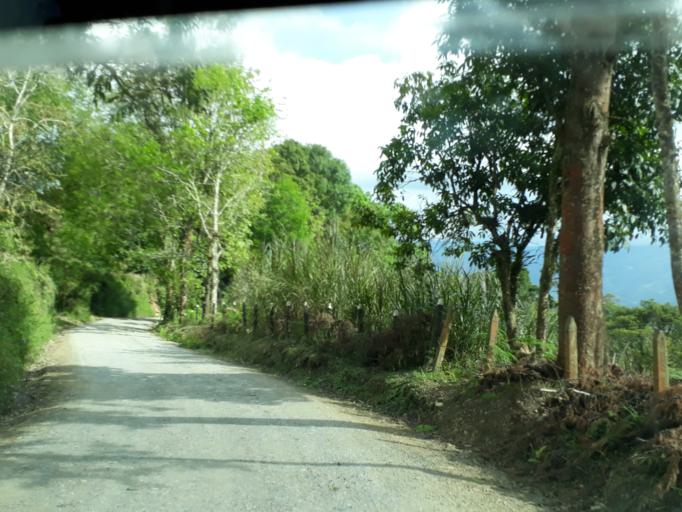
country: CO
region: Cundinamarca
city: Pacho
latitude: 5.2226
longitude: -74.1881
